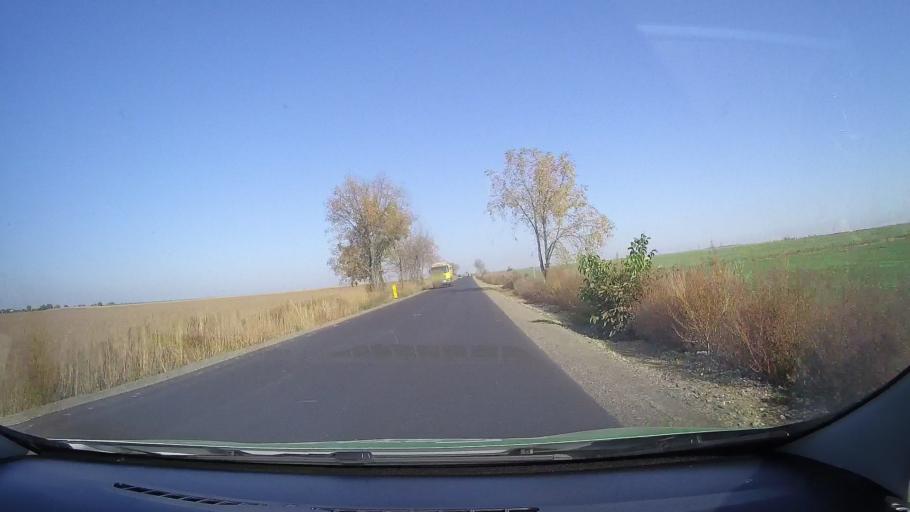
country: RO
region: Satu Mare
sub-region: Comuna Tiream
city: Tiream
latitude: 47.6273
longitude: 22.4677
